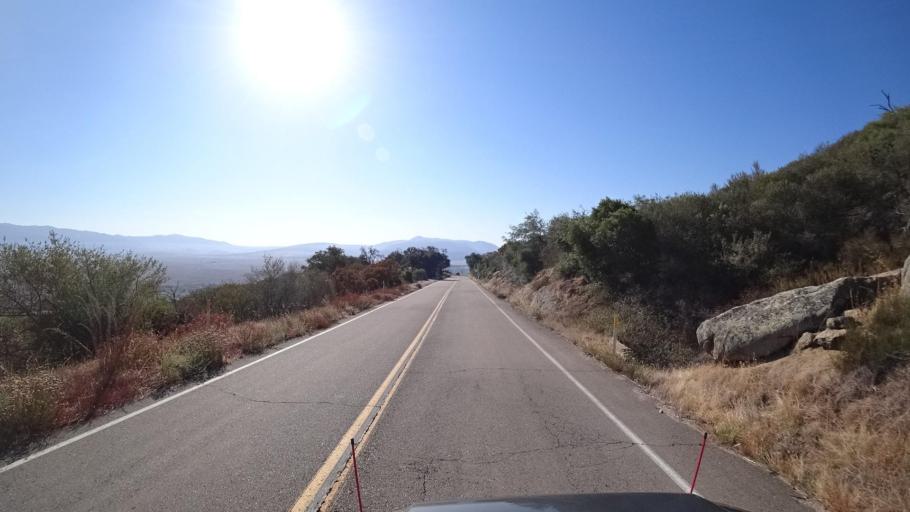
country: US
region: California
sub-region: Riverside County
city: Aguanga
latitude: 33.2567
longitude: -116.7617
